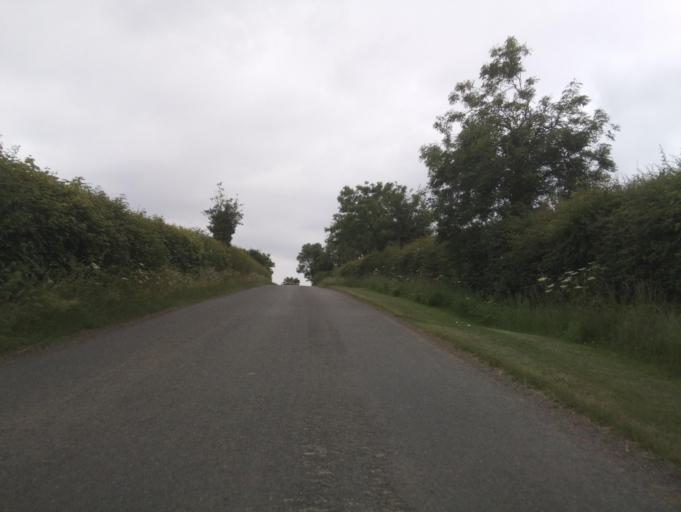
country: GB
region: England
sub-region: District of Rutland
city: Langham
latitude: 52.6718
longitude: -0.7758
